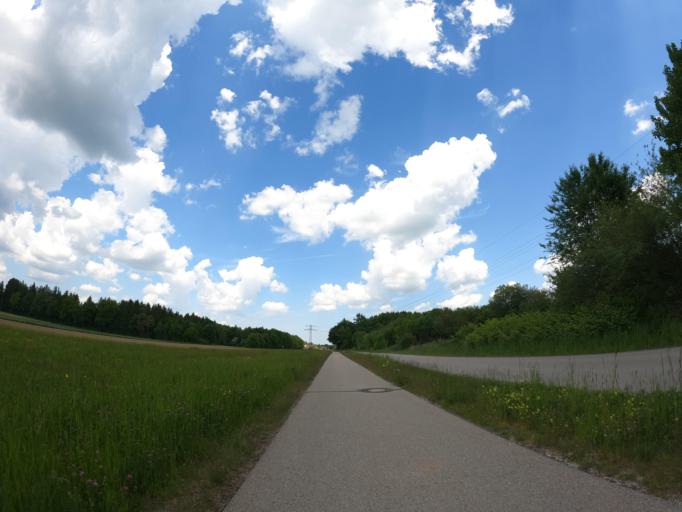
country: DE
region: Bavaria
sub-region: Upper Bavaria
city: Sauerlach
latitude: 47.9870
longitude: 11.6586
